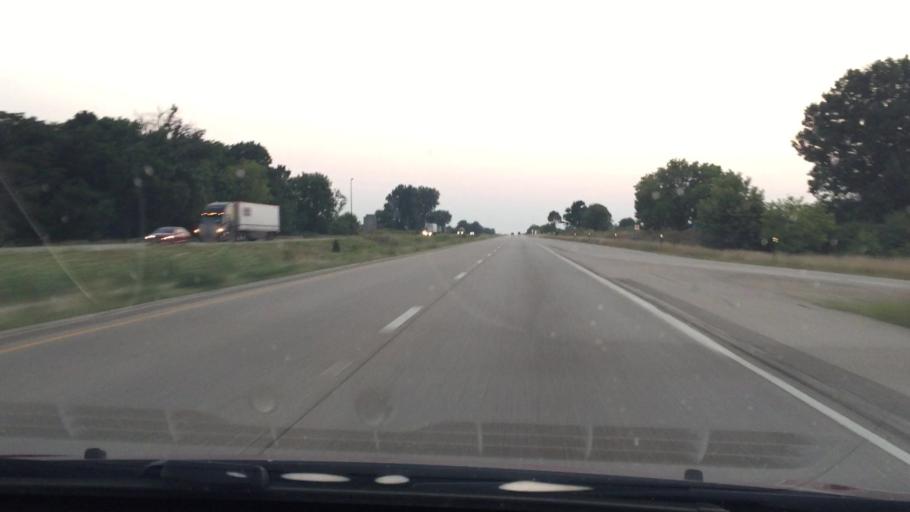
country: US
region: Illinois
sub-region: Bureau County
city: Princeton
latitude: 41.3992
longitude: -89.4727
